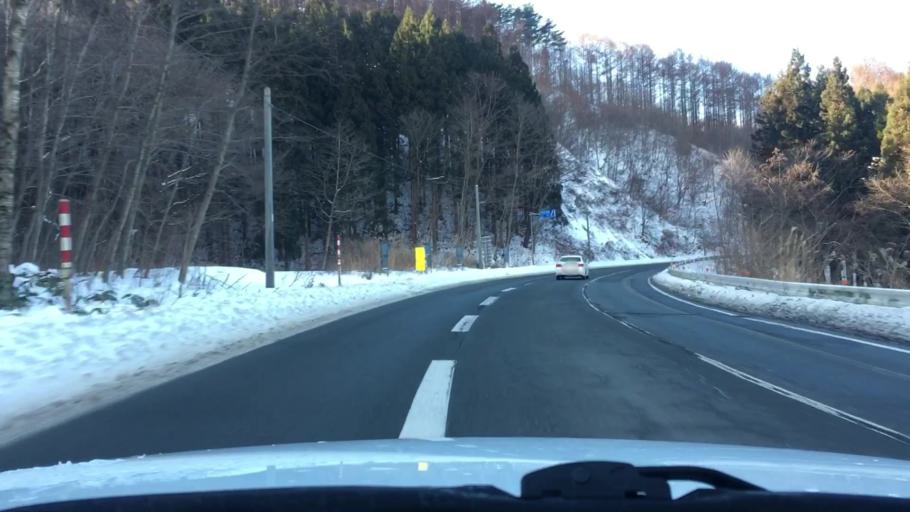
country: JP
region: Iwate
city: Morioka-shi
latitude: 39.6657
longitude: 141.3318
